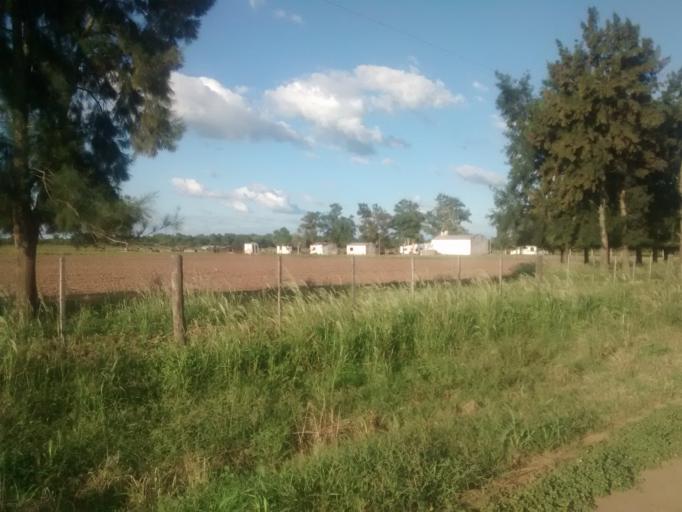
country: AR
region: Chaco
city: Presidencia Roque Saenz Pena
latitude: -26.7369
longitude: -60.3270
